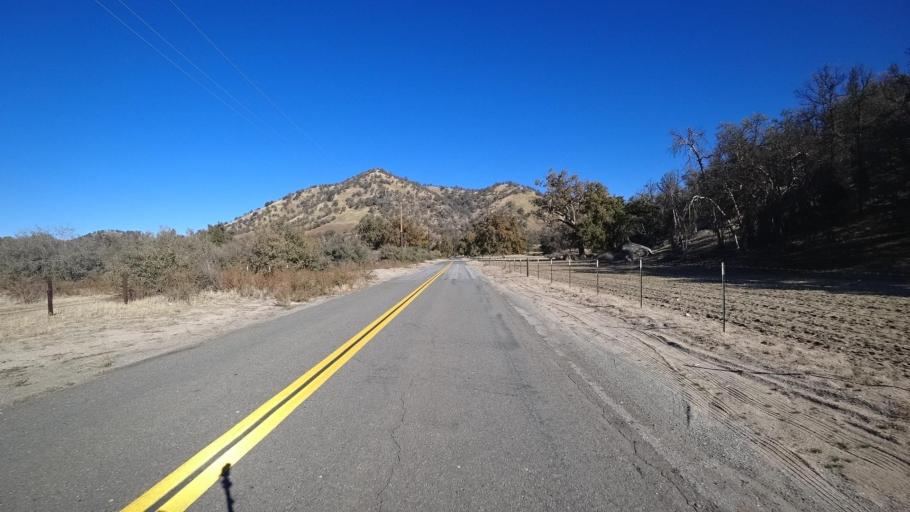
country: US
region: California
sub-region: Kern County
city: Alta Sierra
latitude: 35.7909
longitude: -118.7038
